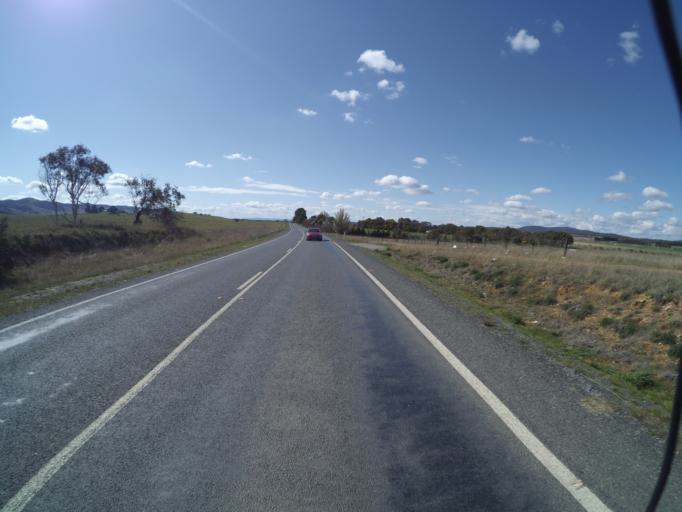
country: AU
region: New South Wales
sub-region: Palerang
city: Bungendore
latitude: -35.2930
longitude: 149.4197
